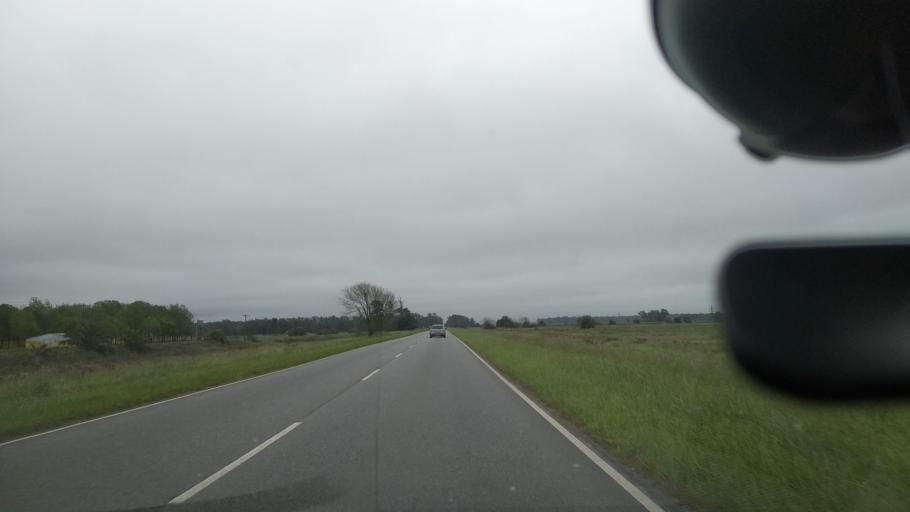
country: AR
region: Buenos Aires
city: Veronica
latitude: -35.3278
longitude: -57.4676
